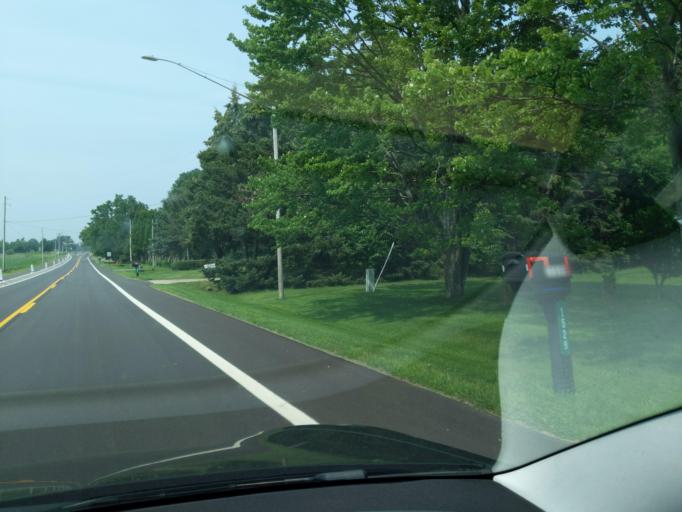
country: US
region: Michigan
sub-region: Clinton County
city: DeWitt
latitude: 42.8244
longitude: -84.5724
